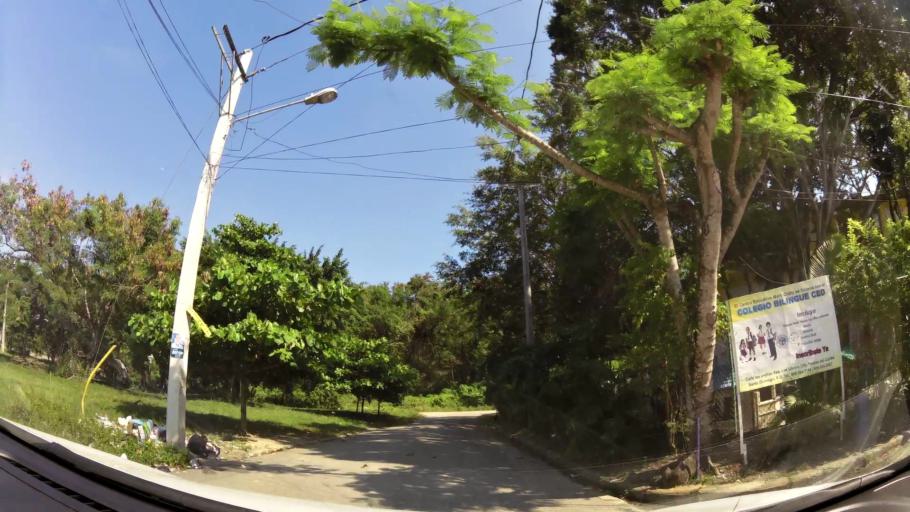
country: DO
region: Santo Domingo
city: Santo Domingo Oeste
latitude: 18.4744
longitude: -70.0073
